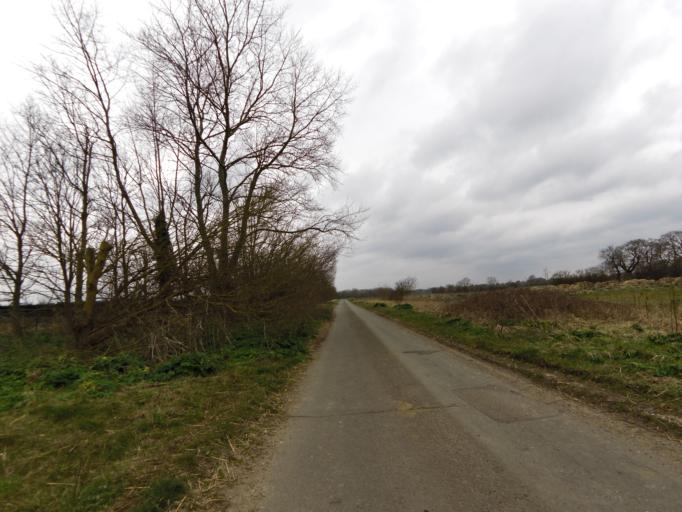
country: GB
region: England
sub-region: Suffolk
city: Halesworth
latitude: 52.3632
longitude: 1.5216
